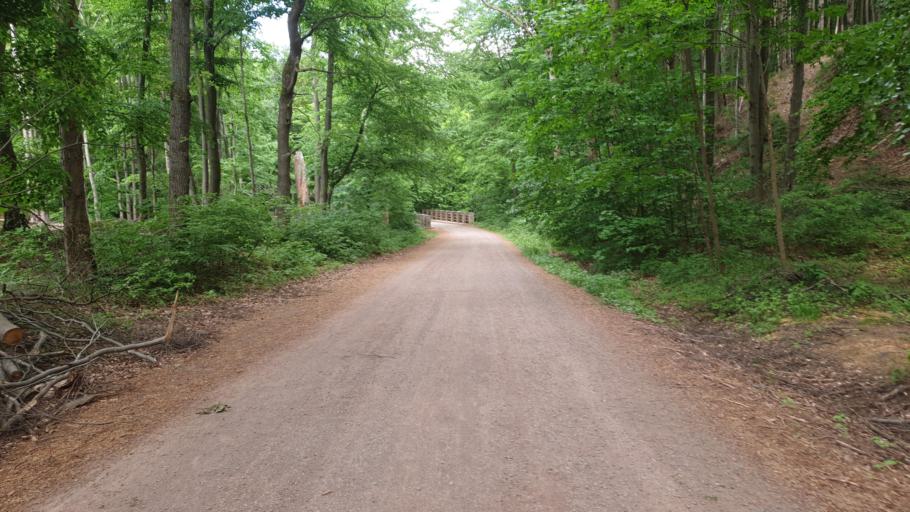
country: DE
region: Saxony-Anhalt
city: Ilsenburg
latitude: 51.8453
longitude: 10.6569
